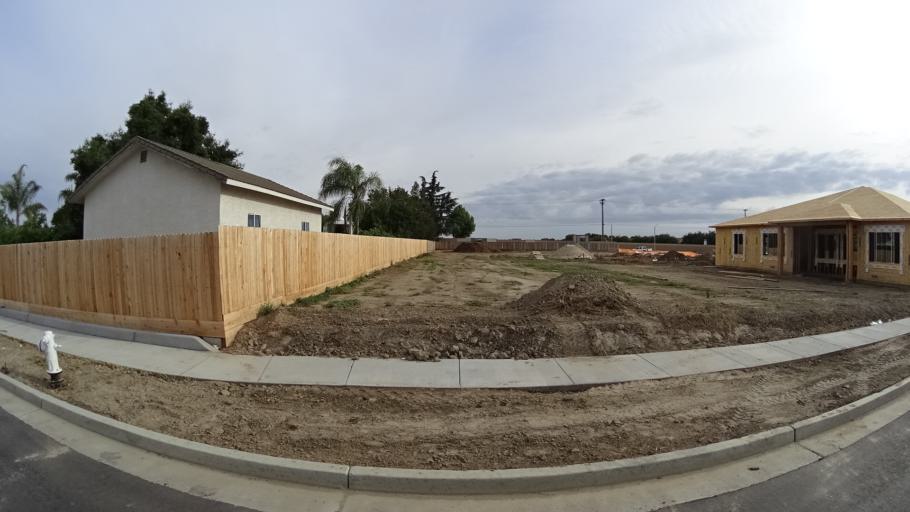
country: US
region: California
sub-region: Kings County
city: Armona
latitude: 36.3413
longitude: -119.6833
